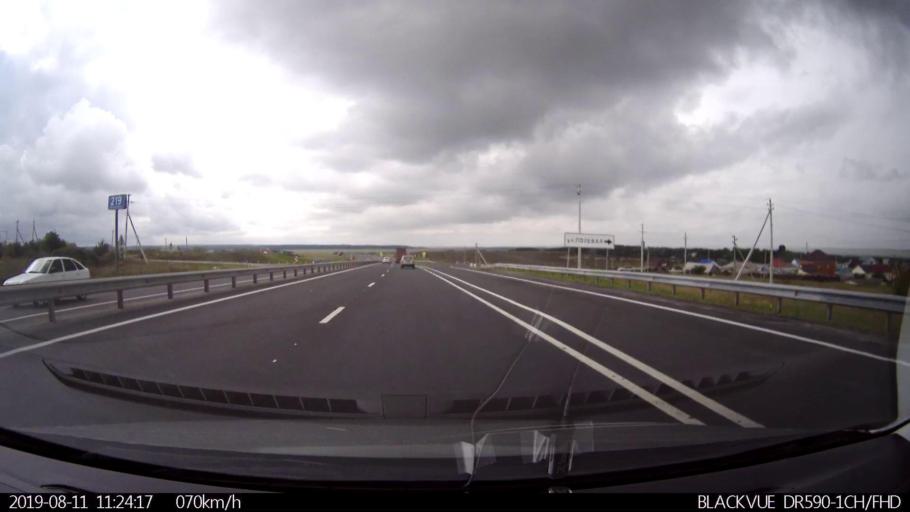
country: RU
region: Ulyanovsk
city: Krasnyy Gulyay
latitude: 54.1287
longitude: 48.2440
